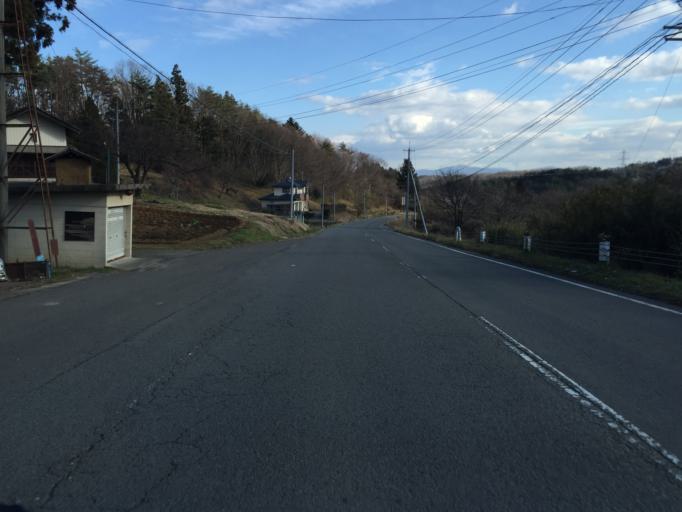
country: JP
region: Fukushima
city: Fukushima-shi
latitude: 37.6856
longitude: 140.4201
